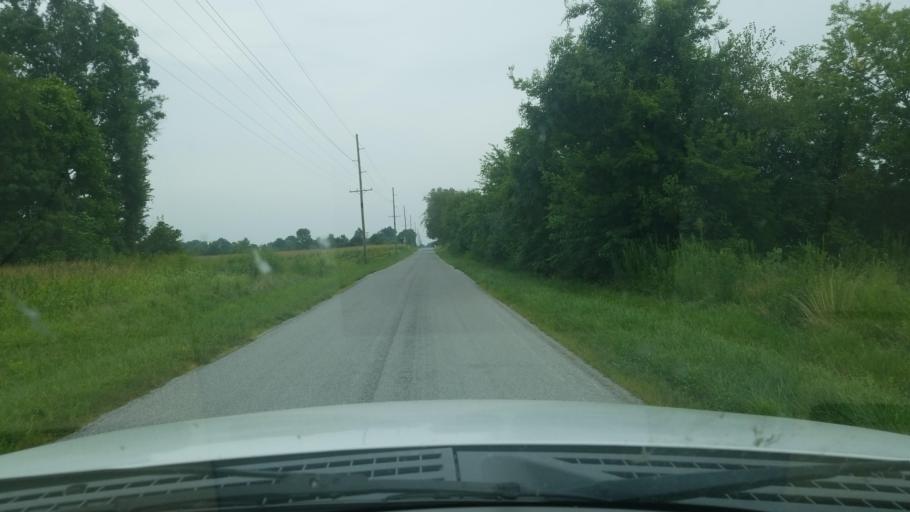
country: US
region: Illinois
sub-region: Saline County
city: Eldorado
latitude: 37.8630
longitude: -88.5168
